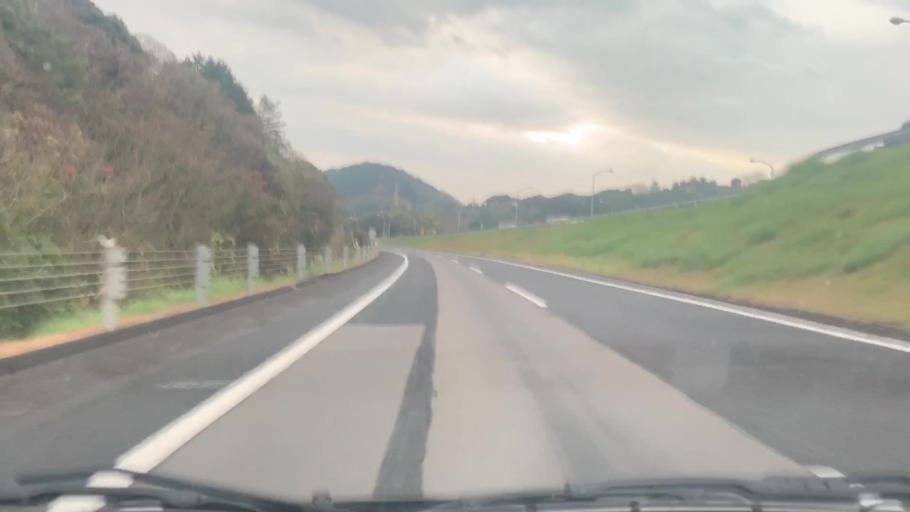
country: JP
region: Nagasaki
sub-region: Isahaya-shi
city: Isahaya
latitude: 32.8627
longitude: 130.0011
